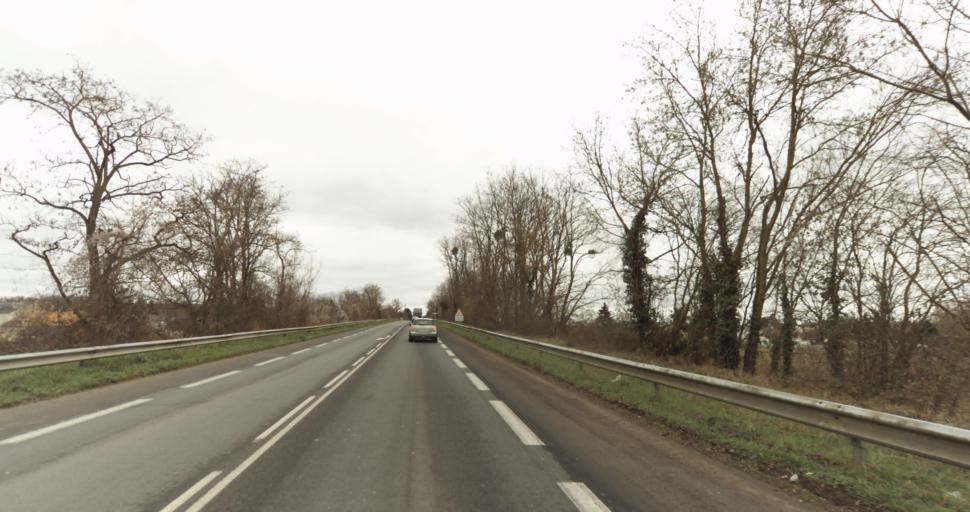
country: FR
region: Pays de la Loire
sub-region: Departement de Maine-et-Loire
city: Varrains
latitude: 47.2359
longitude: -0.0764
